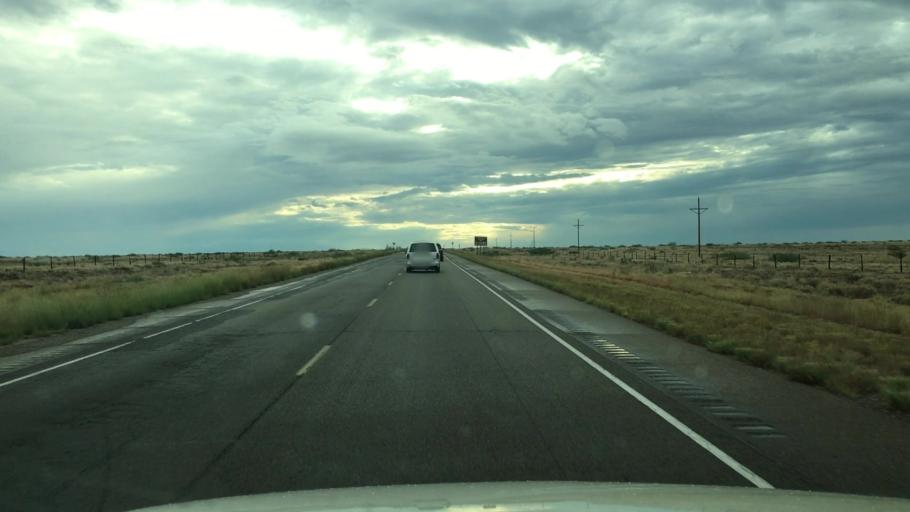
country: US
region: New Mexico
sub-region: Chaves County
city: Roswell
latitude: 33.4024
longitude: -104.3279
